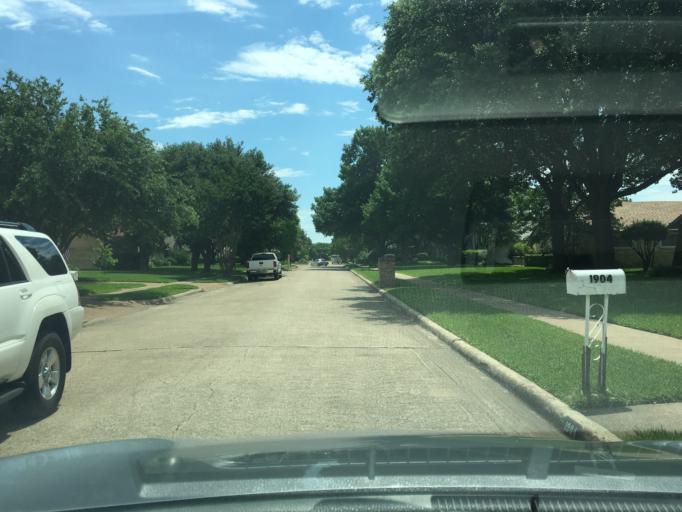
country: US
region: Texas
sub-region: Dallas County
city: Richardson
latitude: 32.9335
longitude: -96.6887
